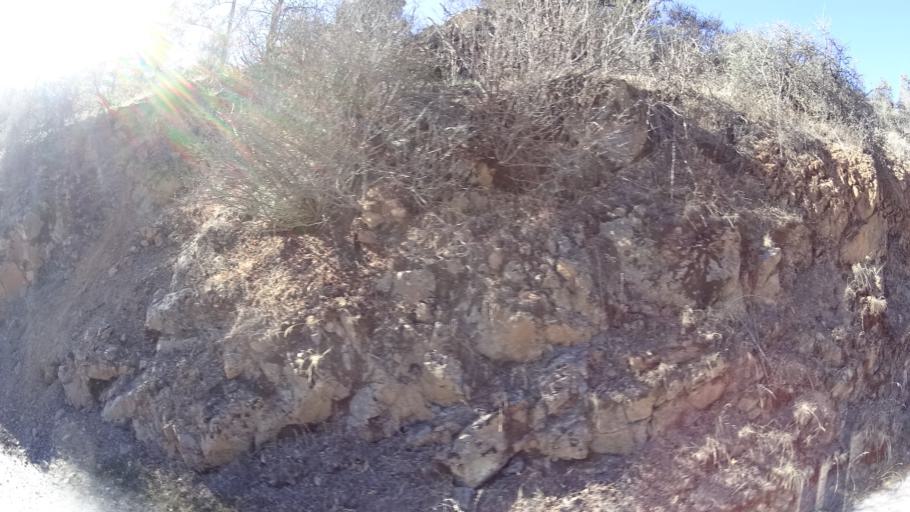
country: US
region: California
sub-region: Siskiyou County
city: Yreka
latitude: 41.8319
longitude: -122.6335
